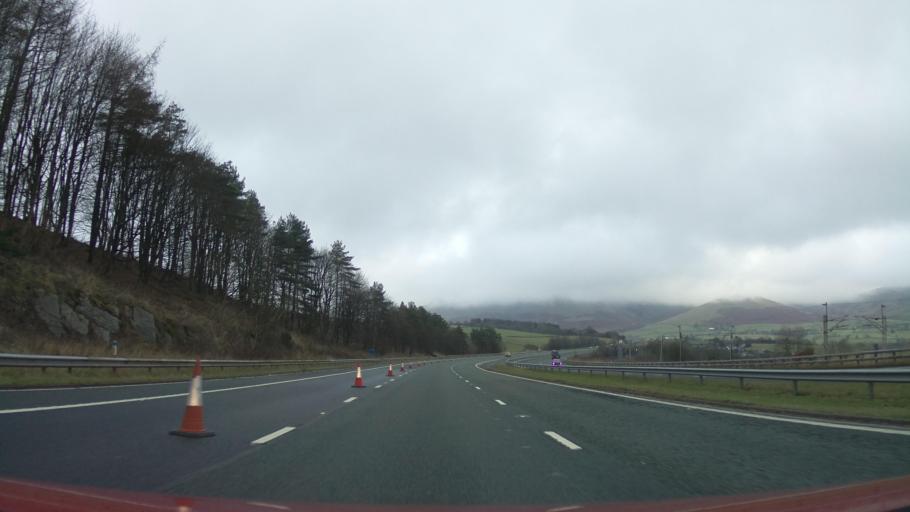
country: GB
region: England
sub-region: Cumbria
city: Sedbergh
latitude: 54.3633
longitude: -2.6030
